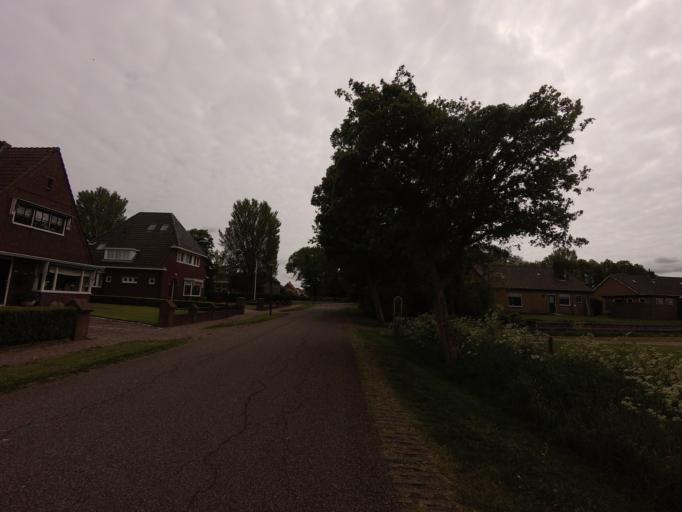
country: NL
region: Friesland
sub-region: Sudwest Fryslan
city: Woudsend
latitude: 52.9442
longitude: 5.6254
